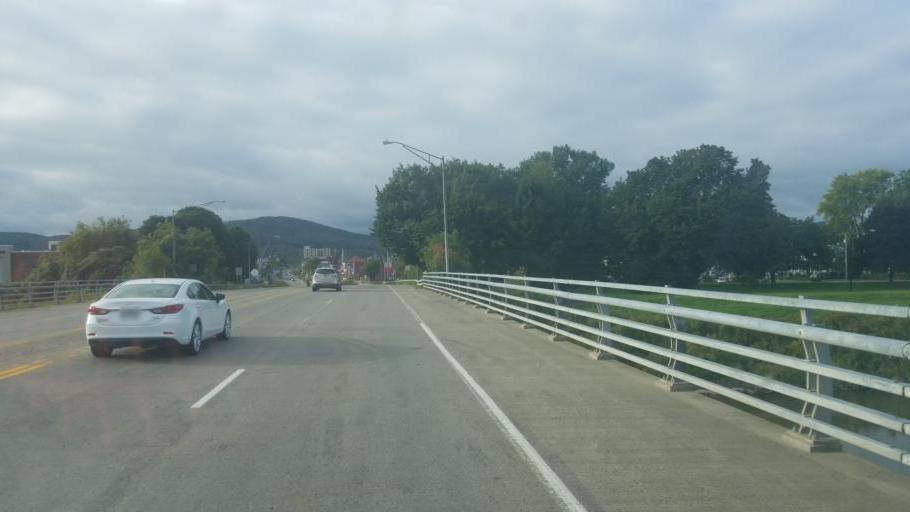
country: US
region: New York
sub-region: Cattaraugus County
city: Olean
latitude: 42.0888
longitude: -78.4299
